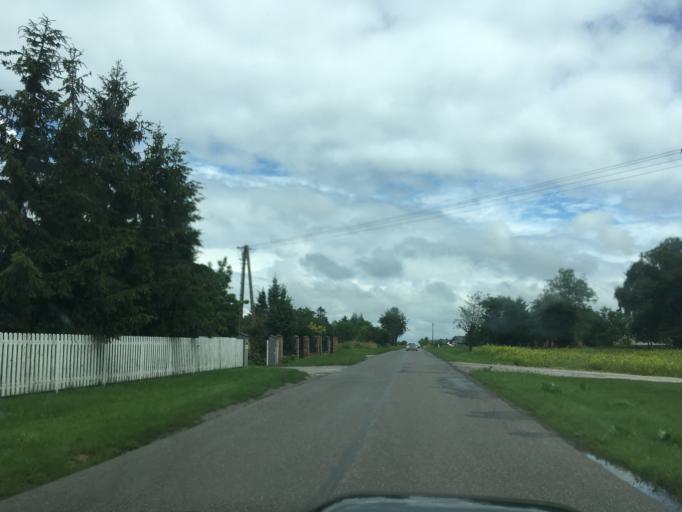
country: PL
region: Lublin Voivodeship
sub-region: Powiat swidnicki
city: Swidnik
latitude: 51.1962
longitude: 22.7184
